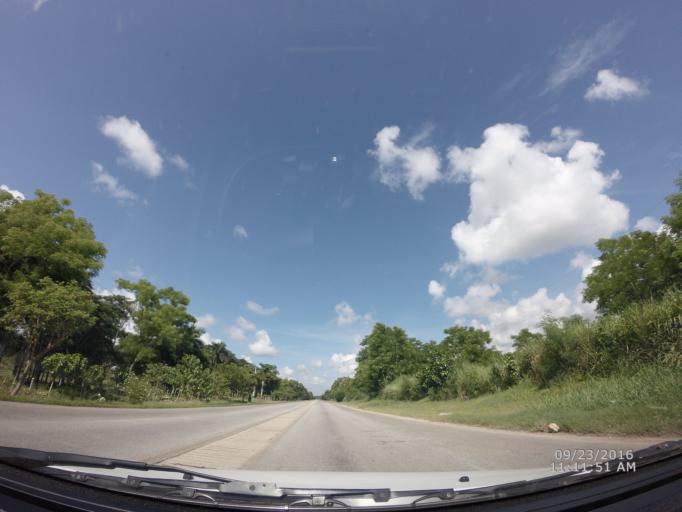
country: CU
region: La Habana
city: Arroyo Naranjo
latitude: 23.0270
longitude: -82.2752
